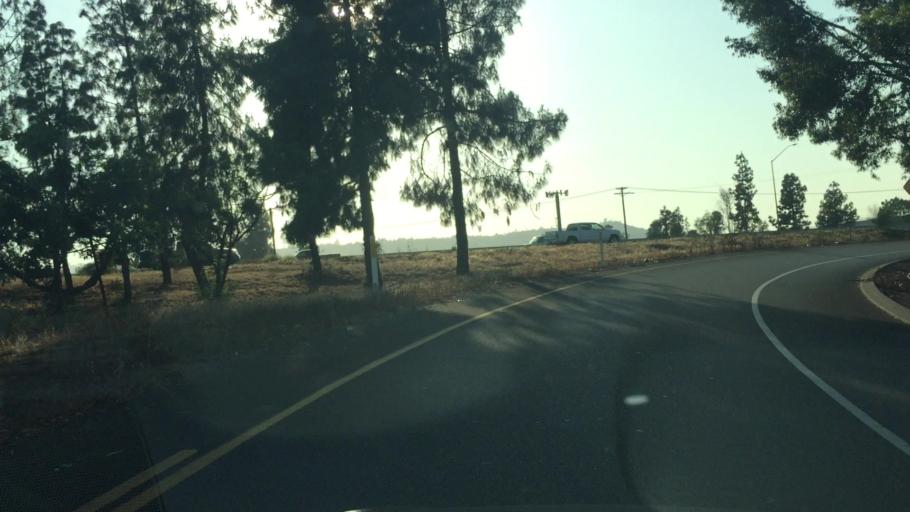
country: US
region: California
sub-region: San Diego County
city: El Cajon
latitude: 32.8087
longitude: -116.9612
